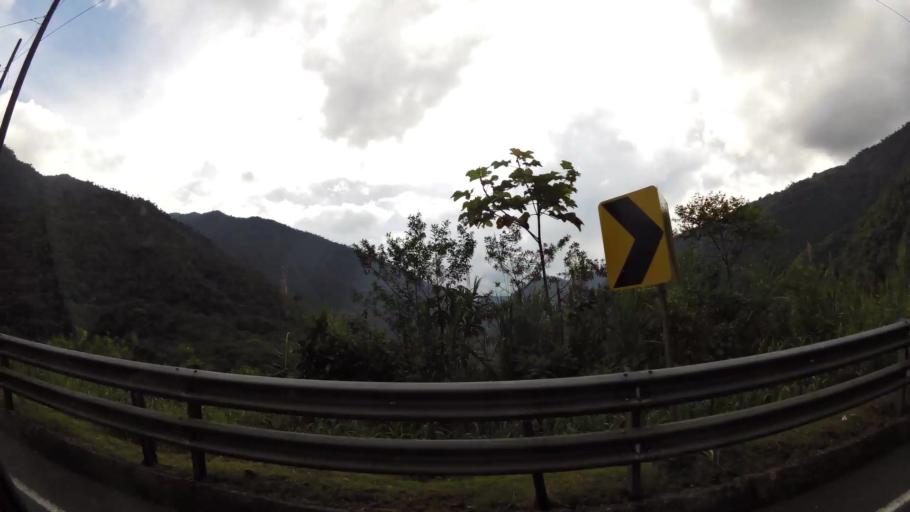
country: EC
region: Pastaza
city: Puyo
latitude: -1.4487
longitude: -78.1597
